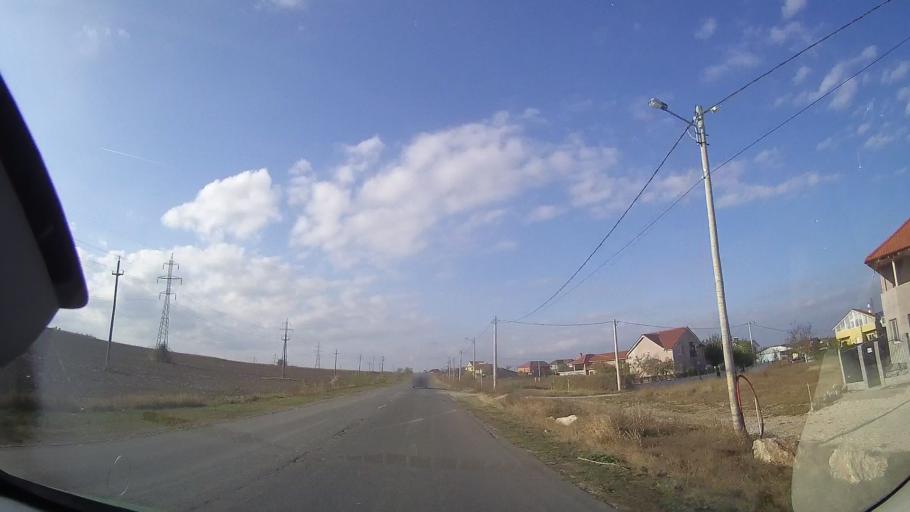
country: RO
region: Constanta
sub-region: Comuna Limanu
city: Limanu
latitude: 43.7913
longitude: 28.5481
